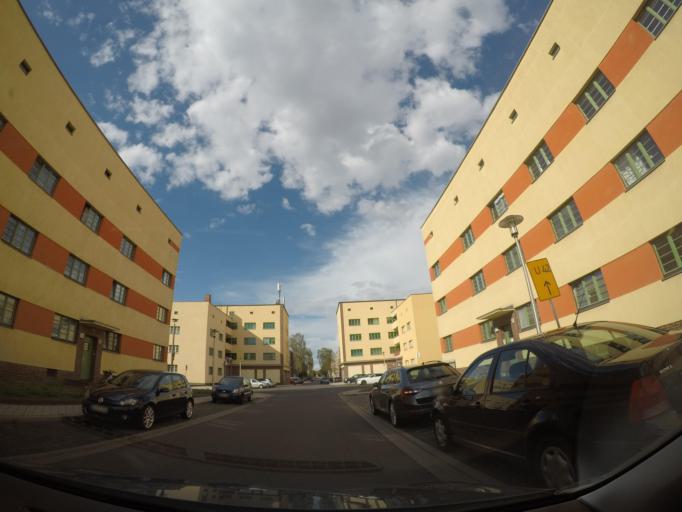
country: DE
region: Saxony-Anhalt
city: Diesdorf
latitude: 52.1240
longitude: 11.5892
